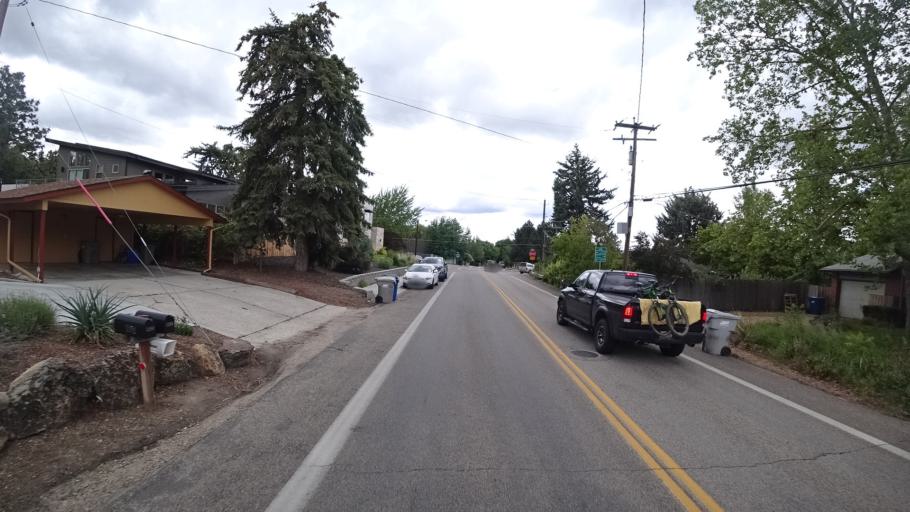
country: US
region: Idaho
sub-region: Ada County
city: Garden City
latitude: 43.6672
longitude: -116.2534
